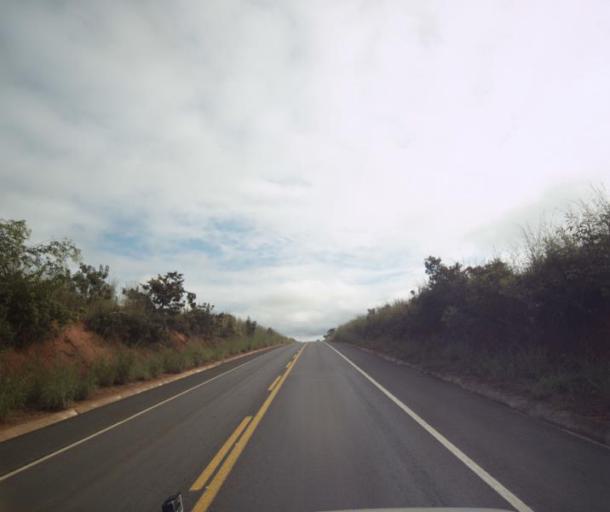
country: BR
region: Goias
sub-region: Padre Bernardo
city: Padre Bernardo
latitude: -15.3661
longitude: -48.6460
